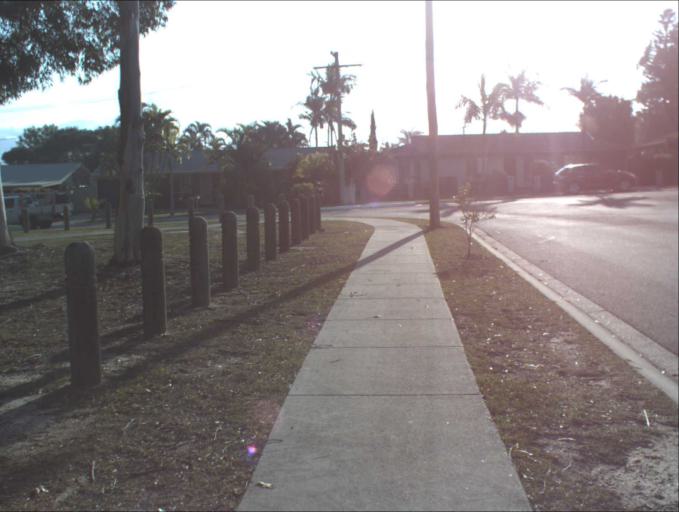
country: AU
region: Queensland
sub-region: Logan
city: Logan Reserve
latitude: -27.6870
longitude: 153.0842
